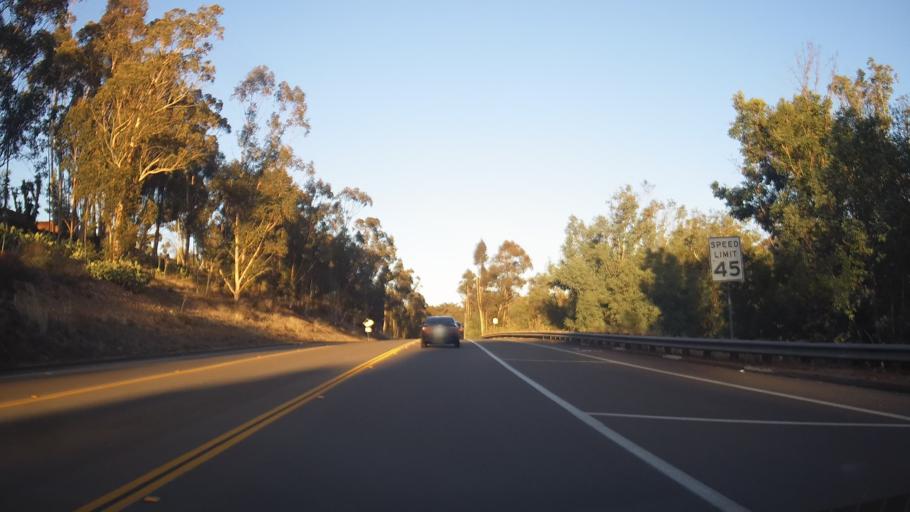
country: US
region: California
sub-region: San Diego County
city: Poway
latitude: 32.9053
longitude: -117.0839
